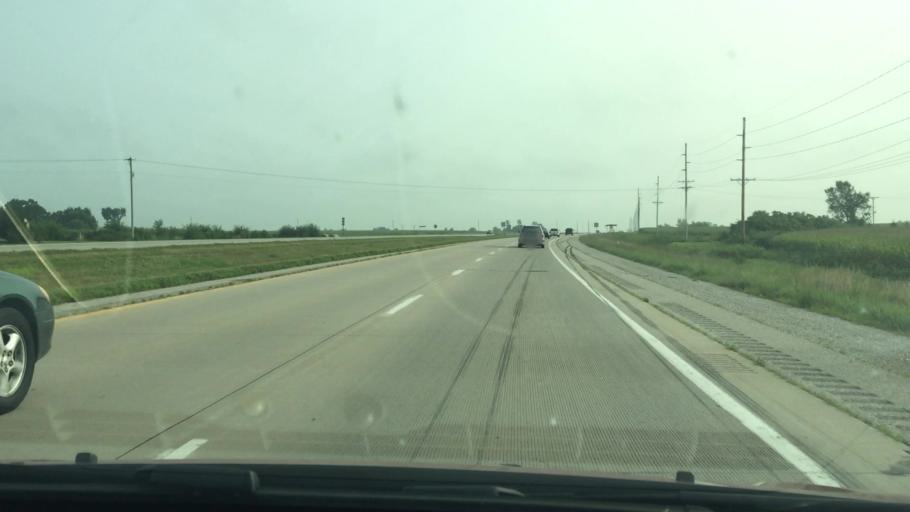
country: US
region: Iowa
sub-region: Muscatine County
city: Muscatine
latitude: 41.4775
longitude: -90.9962
